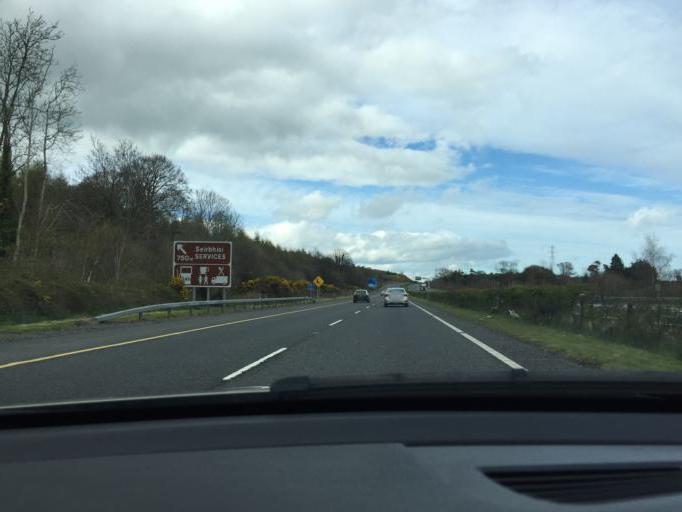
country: IE
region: Leinster
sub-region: Wicklow
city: Ashford
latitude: 53.0289
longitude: -6.0930
